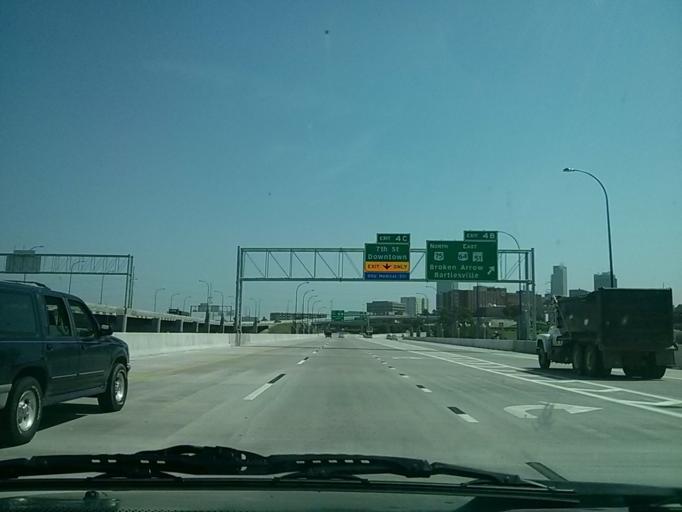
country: US
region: Oklahoma
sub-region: Tulsa County
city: Tulsa
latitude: 36.1429
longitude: -96.0054
